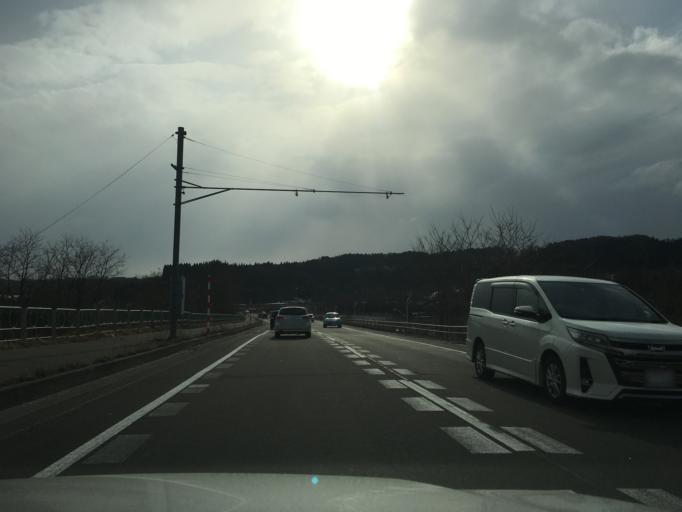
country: JP
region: Aomori
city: Namioka
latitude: 40.7680
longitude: 140.5923
